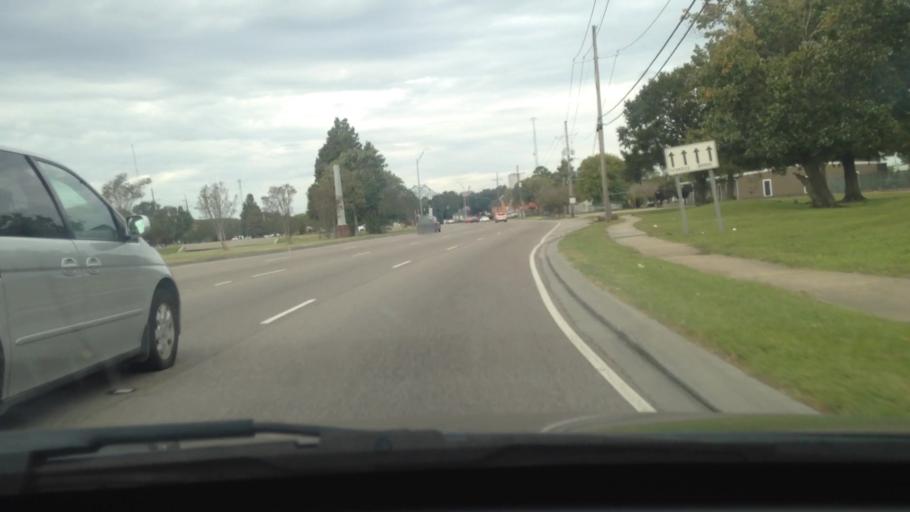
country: US
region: Louisiana
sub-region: Jefferson Parish
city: Terrytown
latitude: 29.9286
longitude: -90.0291
